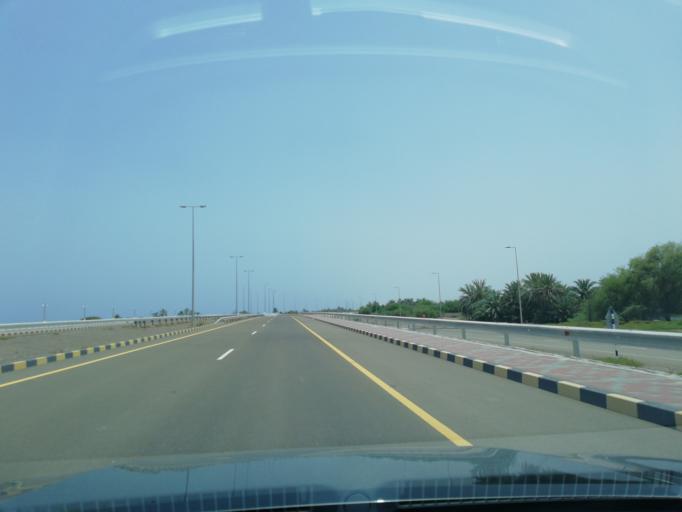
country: OM
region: Al Batinah
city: Shinas
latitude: 24.8054
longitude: 56.4486
